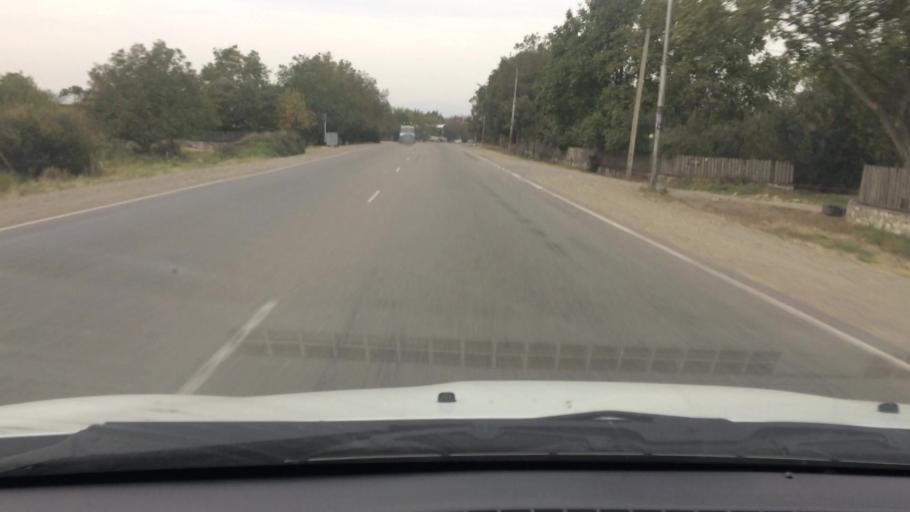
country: GE
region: Kvemo Kartli
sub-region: Marneuli
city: Marneuli
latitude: 41.5865
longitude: 44.7790
